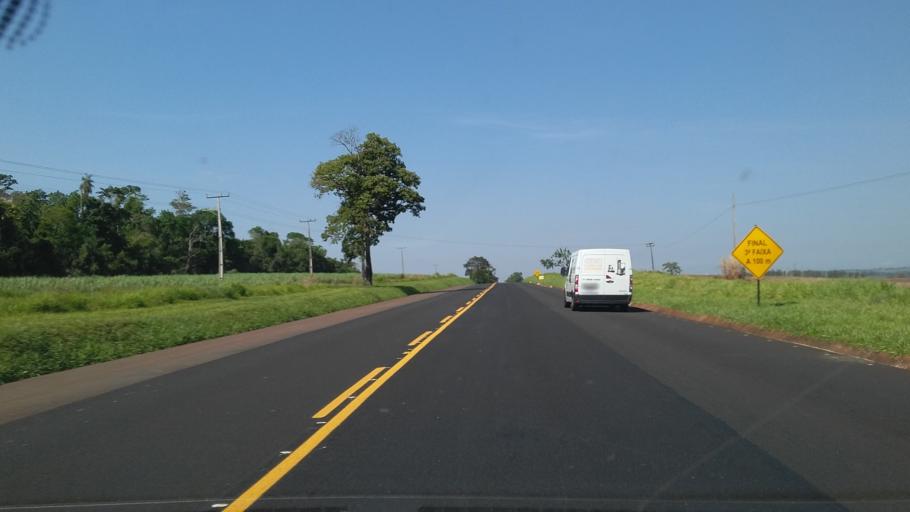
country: BR
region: Parana
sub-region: Bandeirantes
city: Bandeirantes
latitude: -23.1312
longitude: -50.4714
